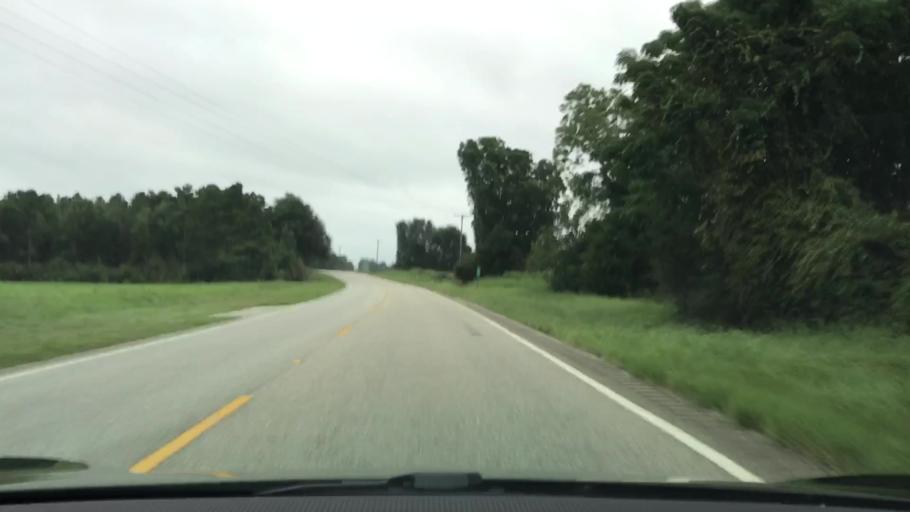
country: US
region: Alabama
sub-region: Coffee County
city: Elba
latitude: 31.3568
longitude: -86.1212
